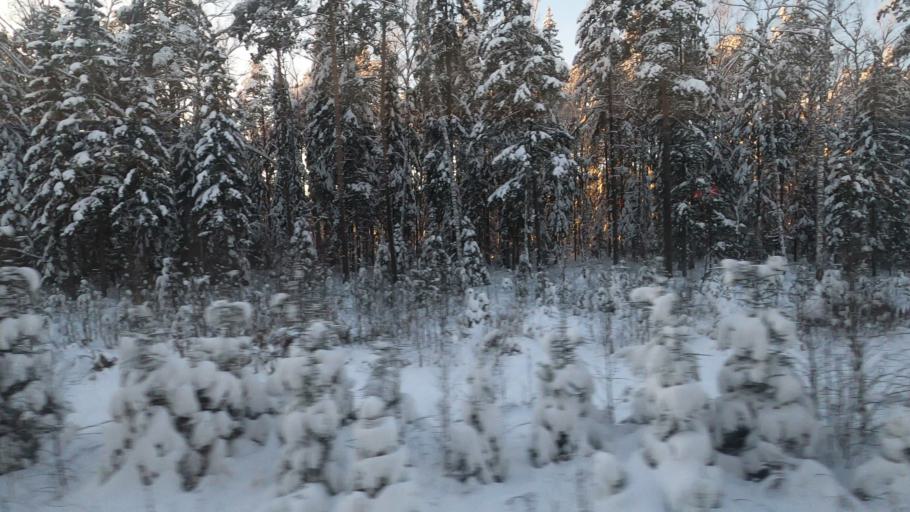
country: RU
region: Moskovskaya
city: Zhukovka
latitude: 56.5091
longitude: 37.5547
